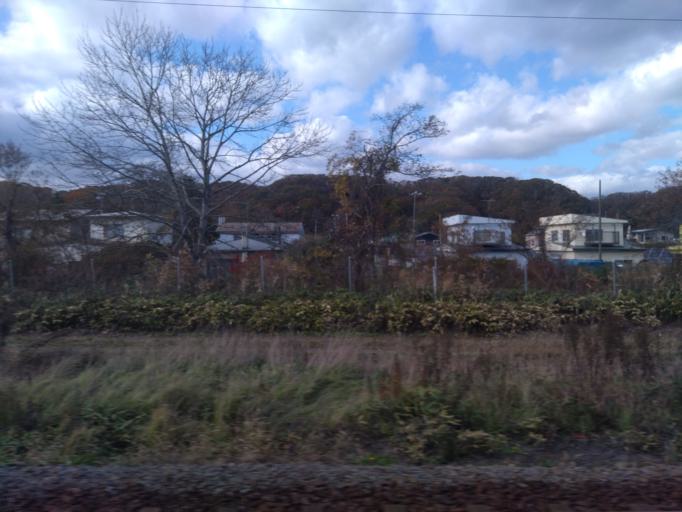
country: JP
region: Hokkaido
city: Shiraoi
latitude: 42.4910
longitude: 141.2572
